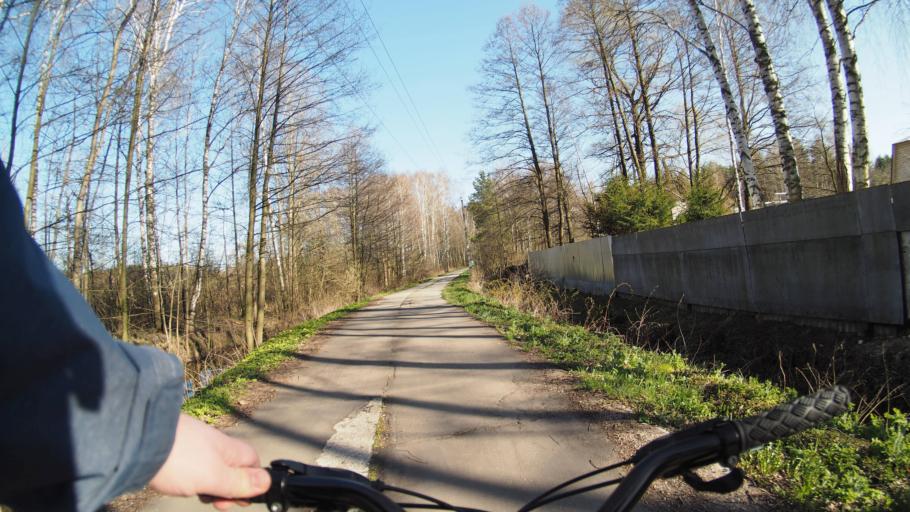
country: RU
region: Moskovskaya
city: Malyshevo
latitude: 55.5208
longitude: 38.3264
